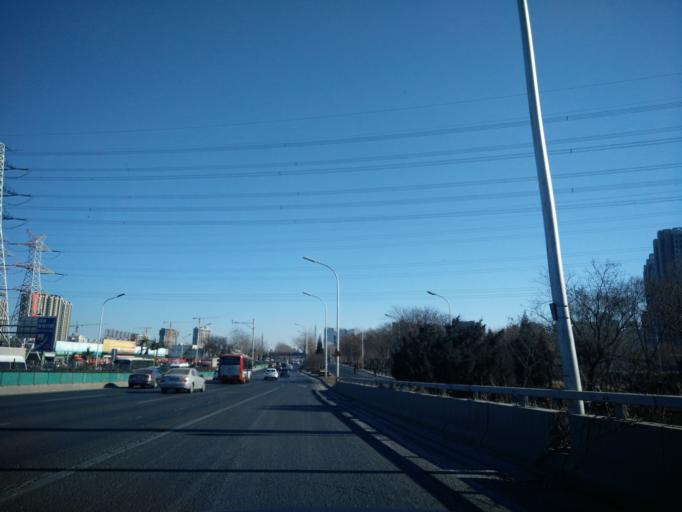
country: CN
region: Beijing
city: Huaxiang
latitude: 39.8494
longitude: 116.3438
